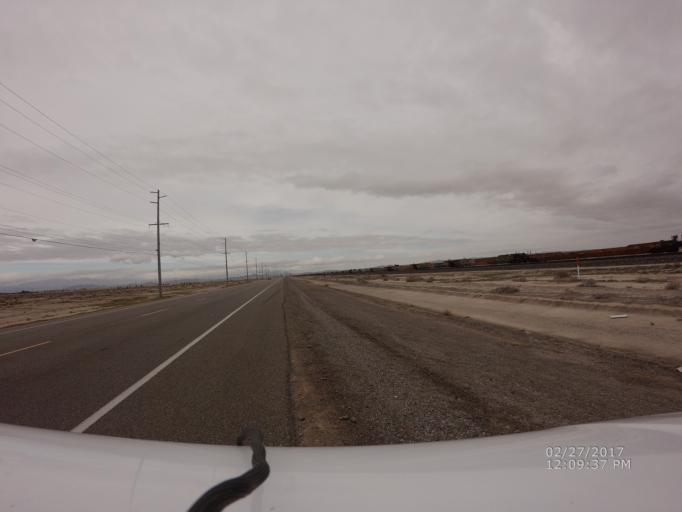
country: US
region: California
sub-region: Los Angeles County
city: Lancaster
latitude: 34.7706
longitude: -118.1481
